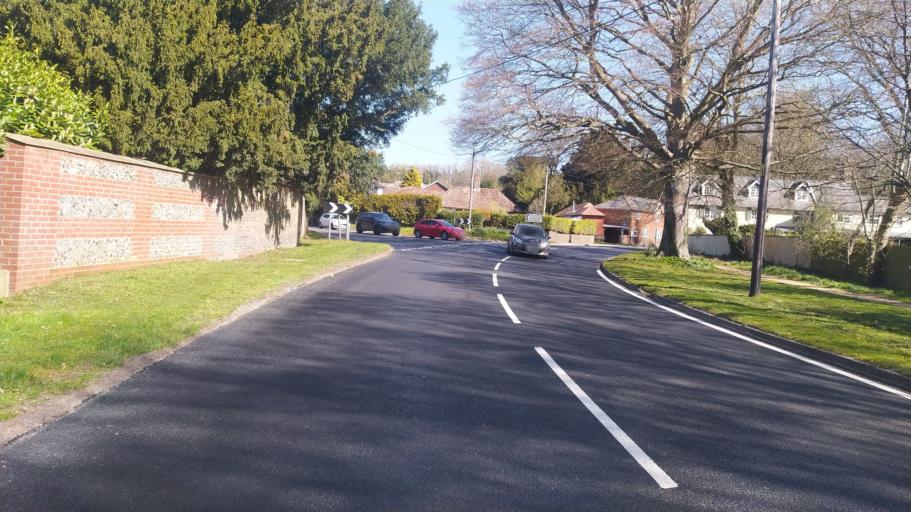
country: GB
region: England
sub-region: Wiltshire
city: Wilton
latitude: 51.0379
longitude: -1.8465
